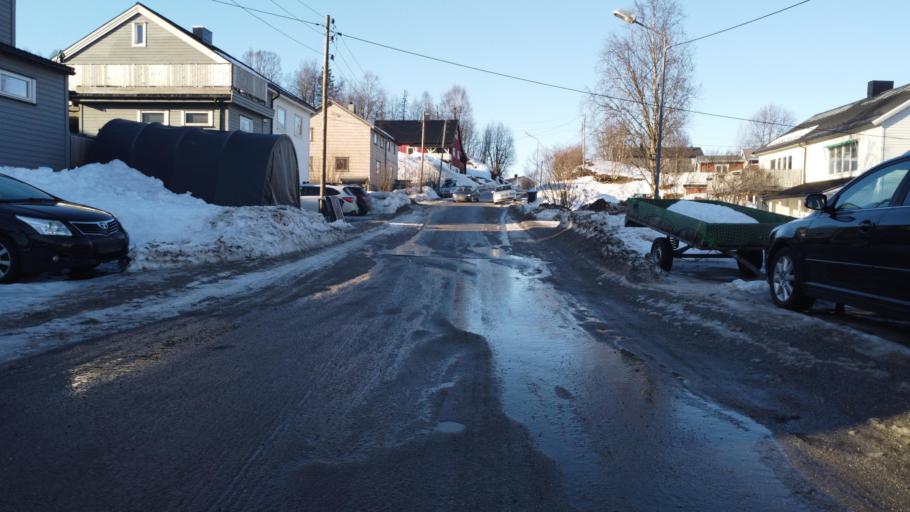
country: NO
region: Nordland
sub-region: Rana
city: Mo i Rana
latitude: 66.3171
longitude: 14.1672
